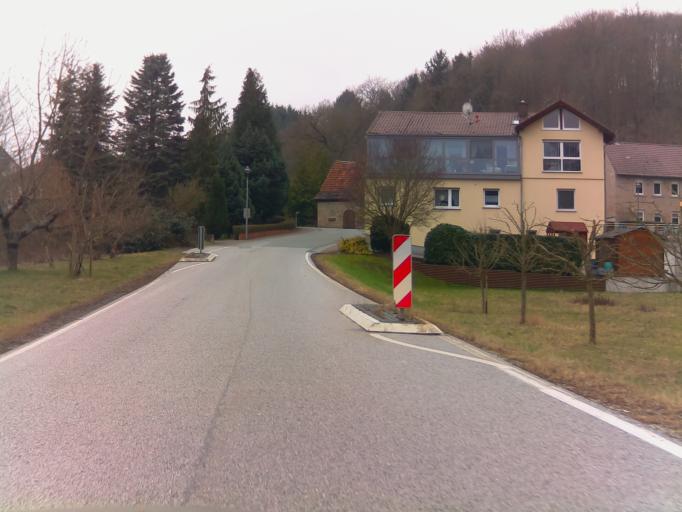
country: DE
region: Rheinland-Pfalz
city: Abtweiler
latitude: 49.7468
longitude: 7.6561
